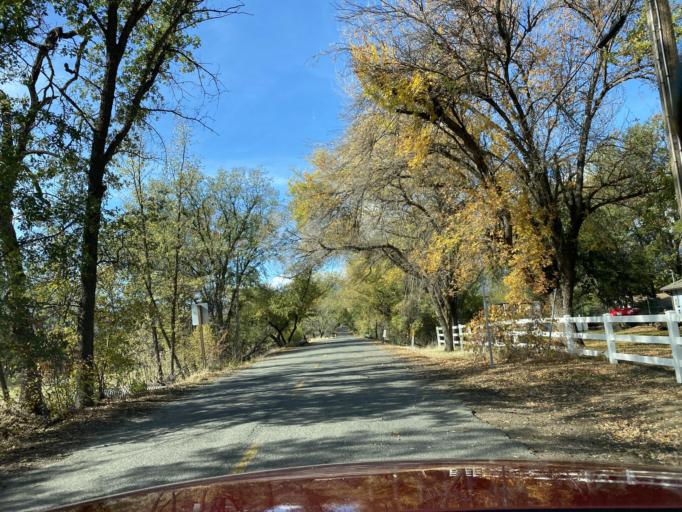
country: US
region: California
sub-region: Lake County
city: Clearlake Oaks
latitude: 39.3778
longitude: -122.5501
